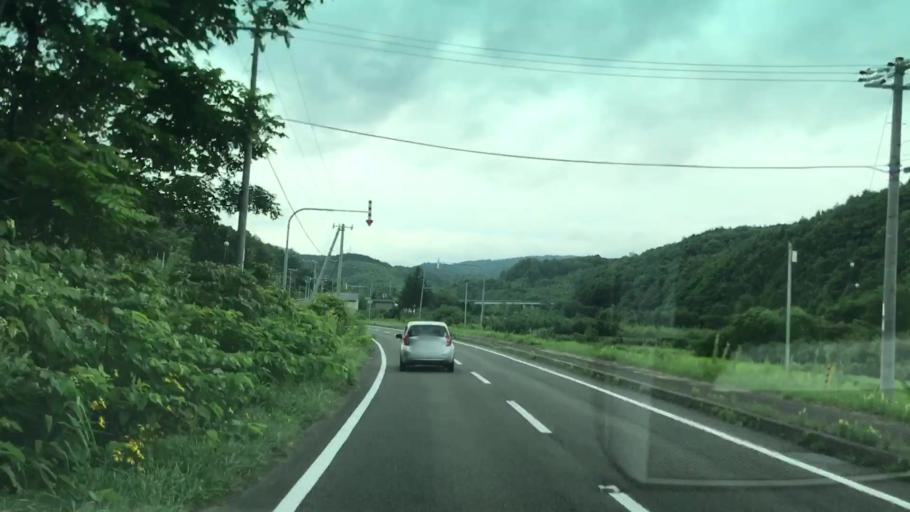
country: JP
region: Hokkaido
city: Yoichi
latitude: 43.1532
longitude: 140.8216
